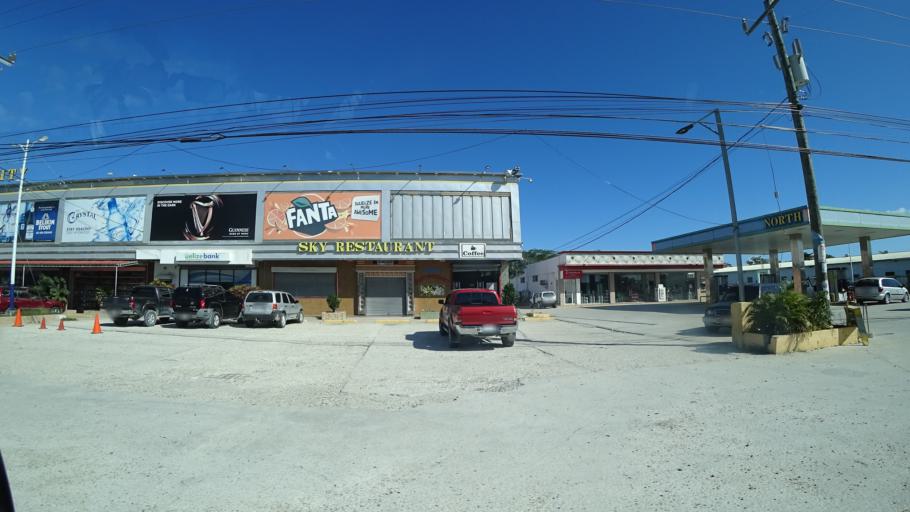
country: BZ
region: Belize
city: Belize City
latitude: 17.5464
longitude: -88.2878
